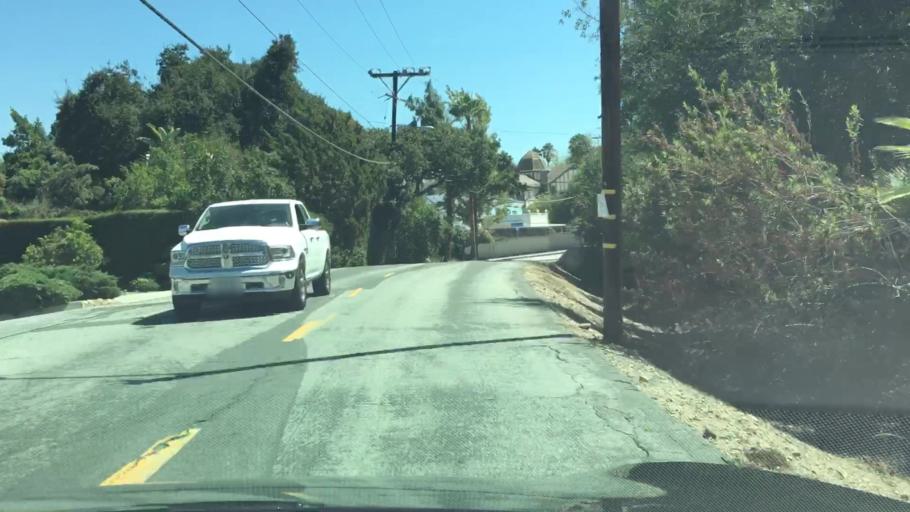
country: US
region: California
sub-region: Los Angeles County
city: Hacienda Heights
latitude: 34.0073
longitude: -117.9887
